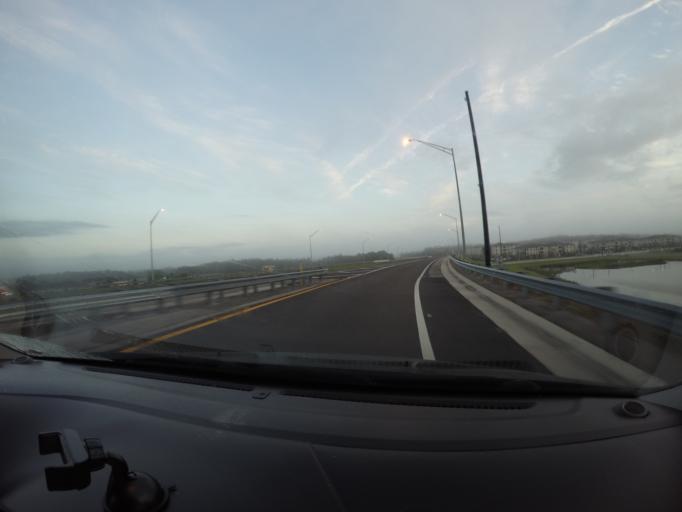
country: US
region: Florida
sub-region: Orange County
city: Conway
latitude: 28.4125
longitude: -81.2282
